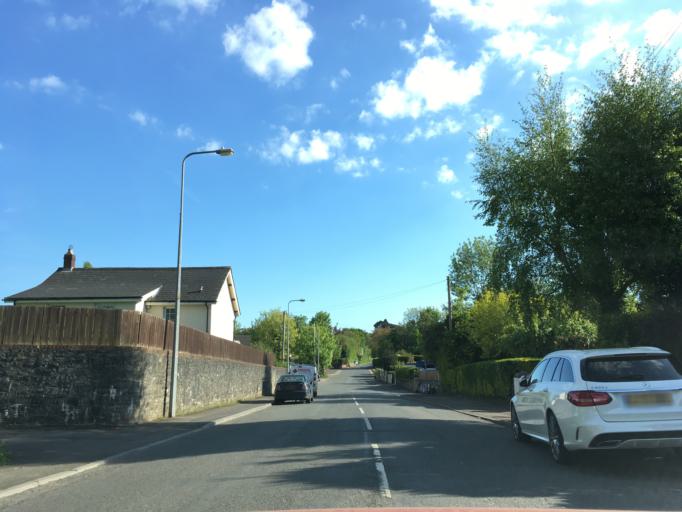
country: GB
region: Wales
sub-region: Newport
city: Marshfield
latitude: 51.5320
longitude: -3.1118
